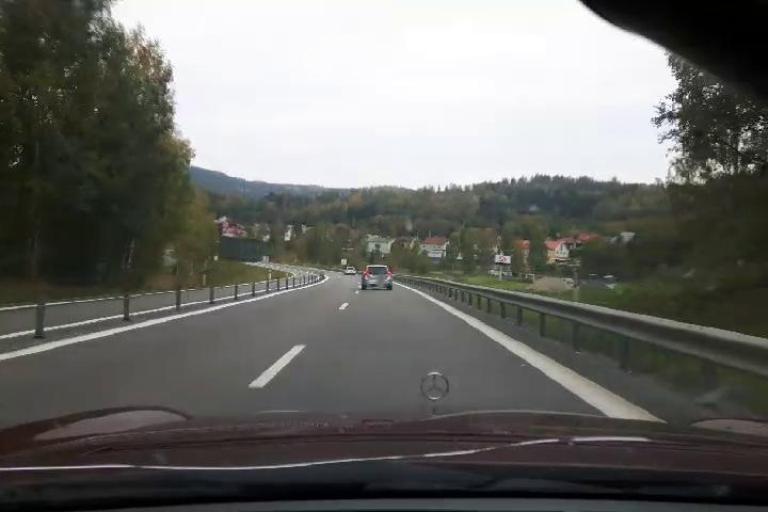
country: SE
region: Vaesternorrland
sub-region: Kramfors Kommun
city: Nordingra
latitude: 63.0521
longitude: 18.3267
